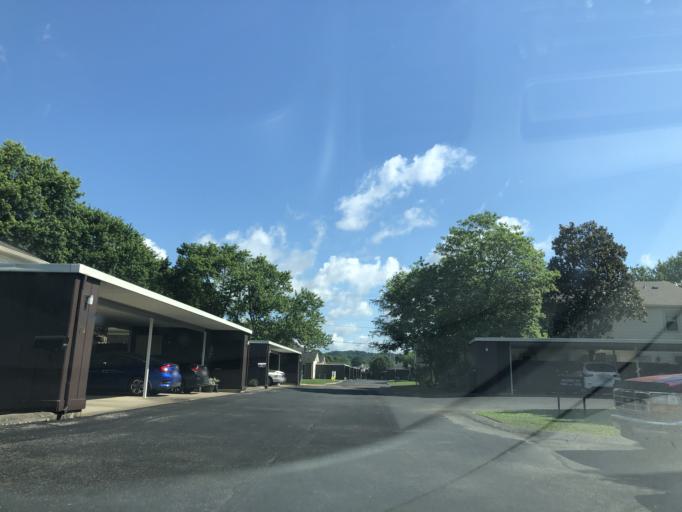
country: US
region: Tennessee
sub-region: Davidson County
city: Belle Meade
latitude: 36.0681
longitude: -86.9526
